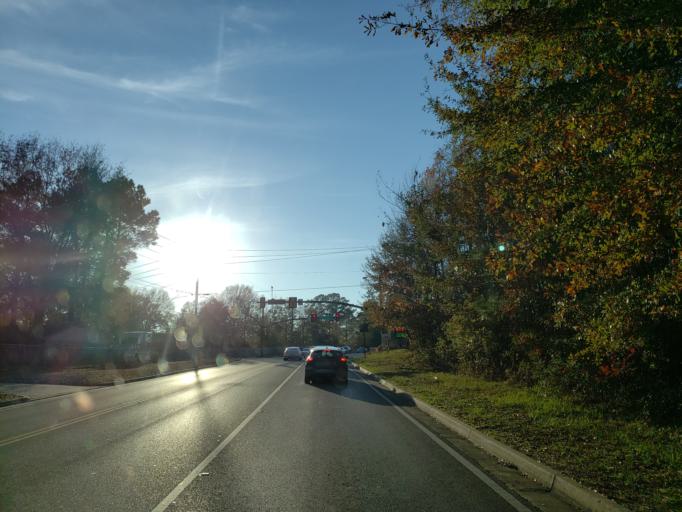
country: US
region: Mississippi
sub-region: Lamar County
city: Arnold Line
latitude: 31.3371
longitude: -89.3564
